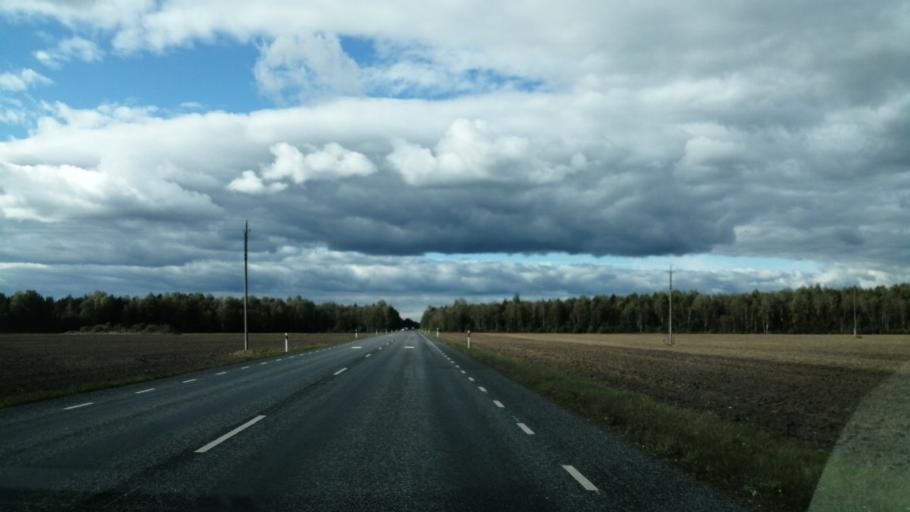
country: EE
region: Jaervamaa
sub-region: Tueri vald
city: Sarevere
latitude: 58.7628
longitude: 25.5460
